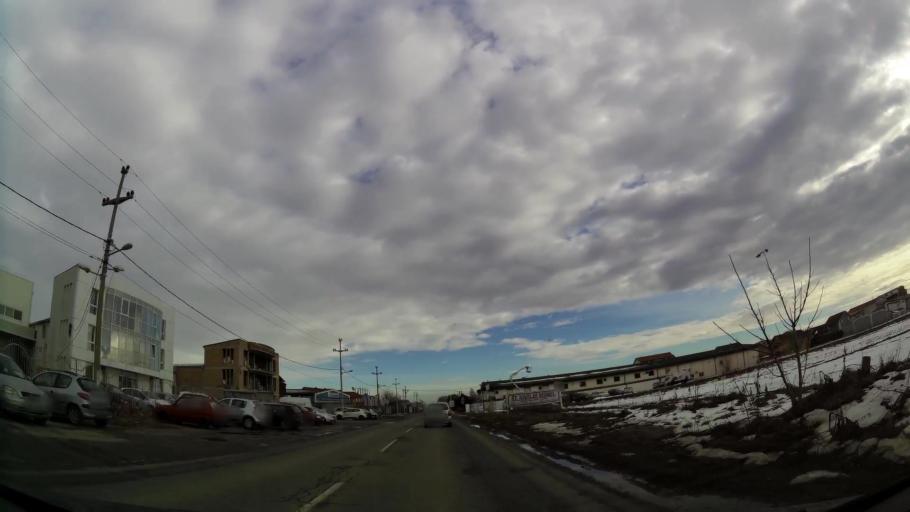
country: RS
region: Central Serbia
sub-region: Belgrade
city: Surcin
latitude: 44.8024
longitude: 20.3394
